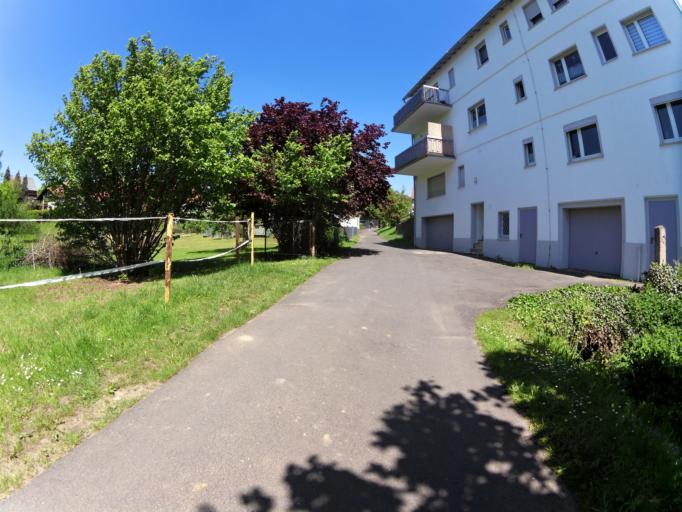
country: DE
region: Thuringia
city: Dankmarshausen
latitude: 50.9503
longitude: 9.9931
